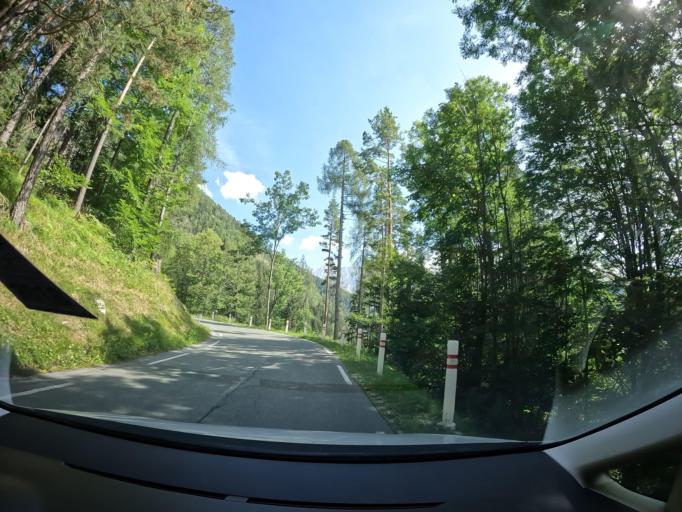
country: AT
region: Carinthia
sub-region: Politischer Bezirk Feldkirchen
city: Glanegg
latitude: 46.7254
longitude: 14.2384
